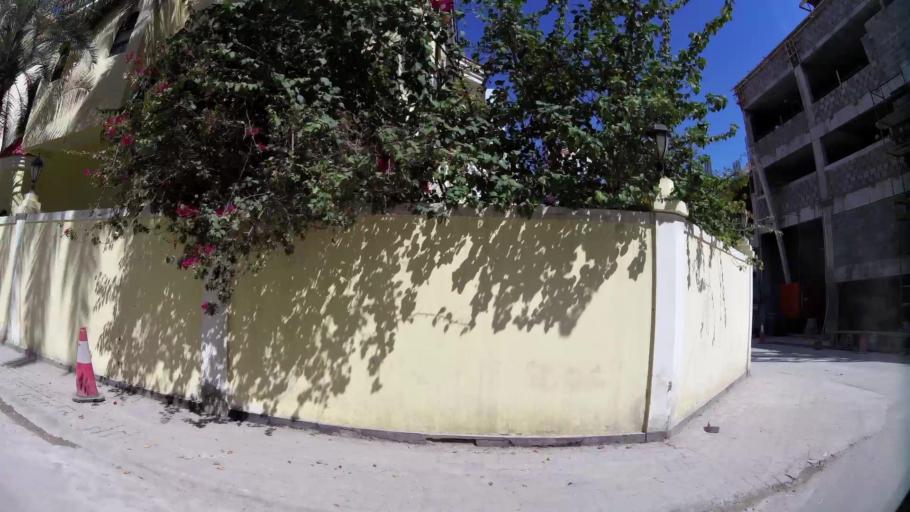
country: BH
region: Manama
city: Manama
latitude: 26.2136
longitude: 50.6026
